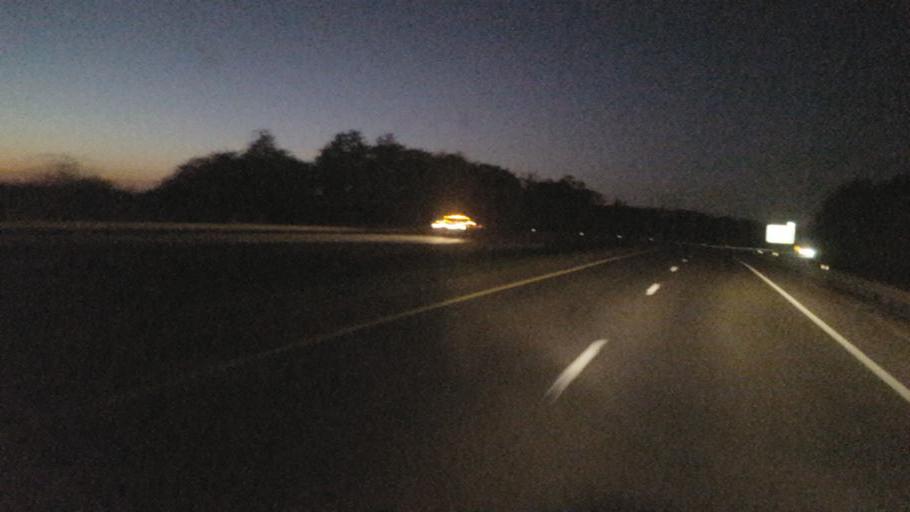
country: US
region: Ohio
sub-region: Pickaway County
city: Circleville
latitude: 39.5924
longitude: -82.9544
